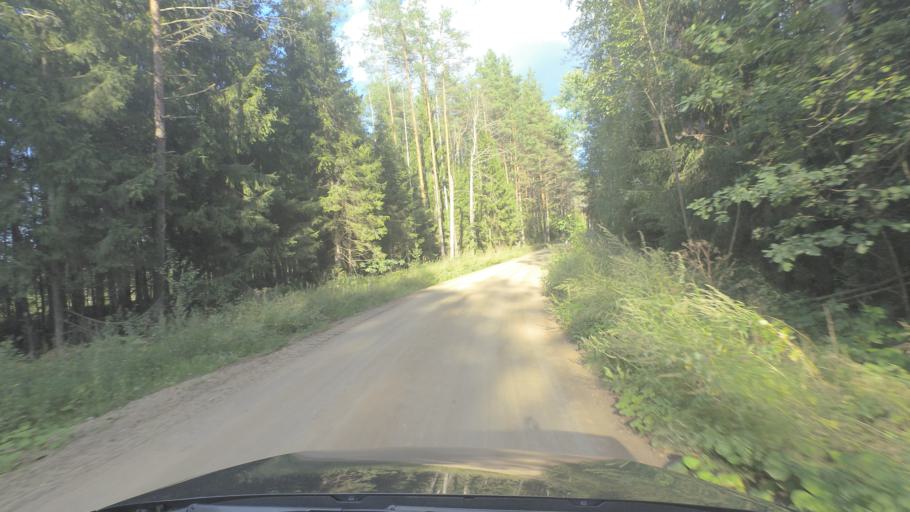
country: LT
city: Pabrade
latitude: 55.1484
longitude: 25.7503
